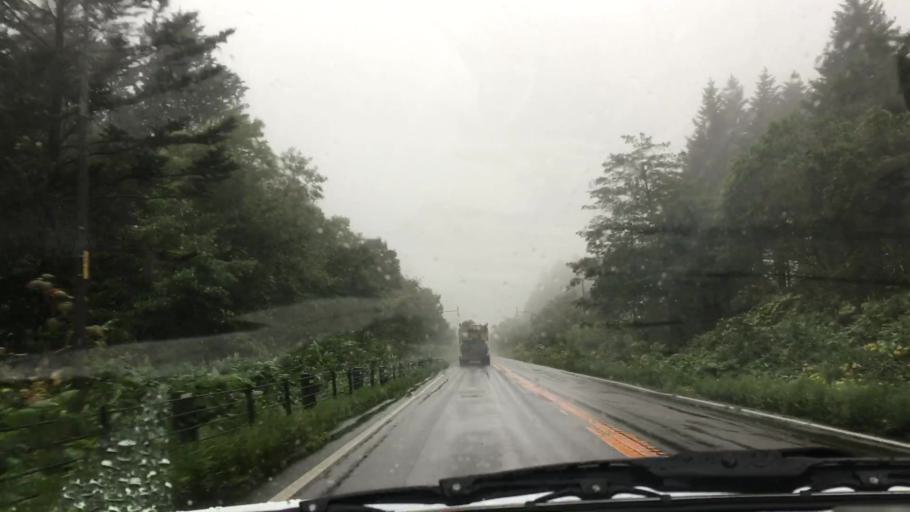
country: JP
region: Hokkaido
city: Niseko Town
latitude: 42.5931
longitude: 140.5125
